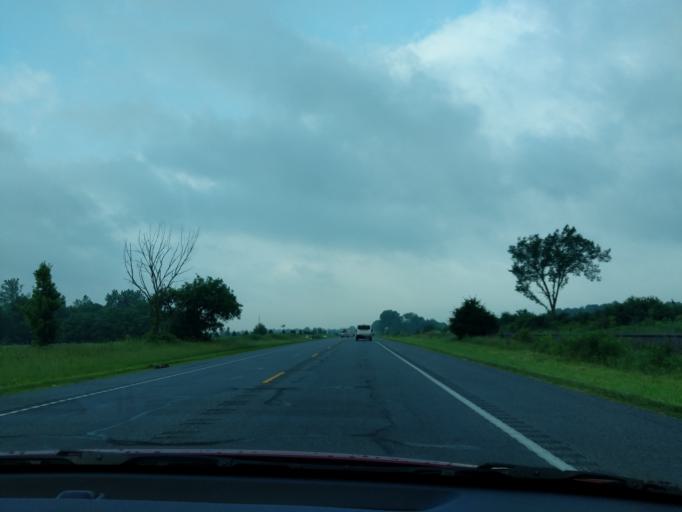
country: US
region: Indiana
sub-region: Hancock County
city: McCordsville
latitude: 39.9055
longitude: -85.9023
